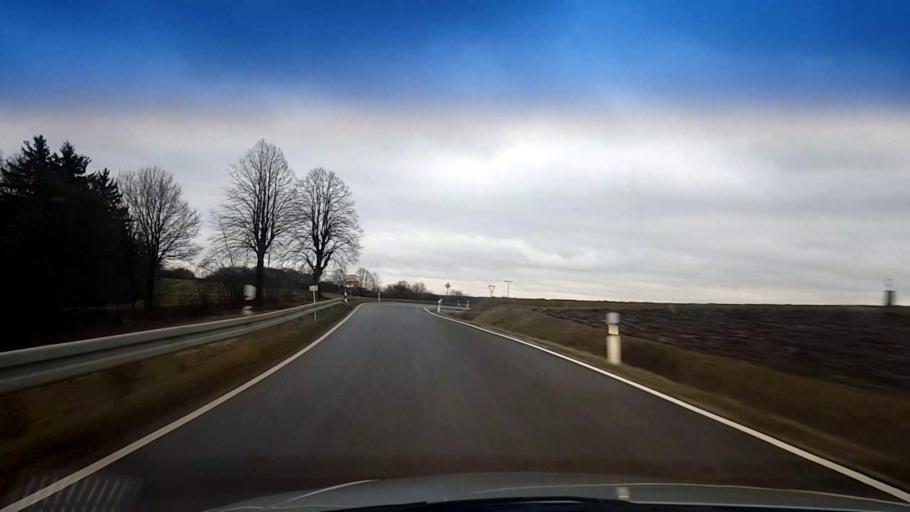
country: DE
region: Bavaria
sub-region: Upper Franconia
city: Wattendorf
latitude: 50.0280
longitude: 11.0655
